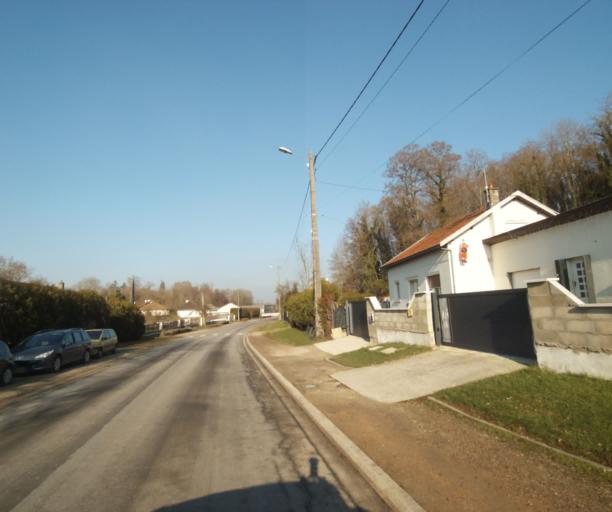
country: FR
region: Champagne-Ardenne
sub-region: Departement de la Haute-Marne
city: Wassy
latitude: 48.4751
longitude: 4.9705
